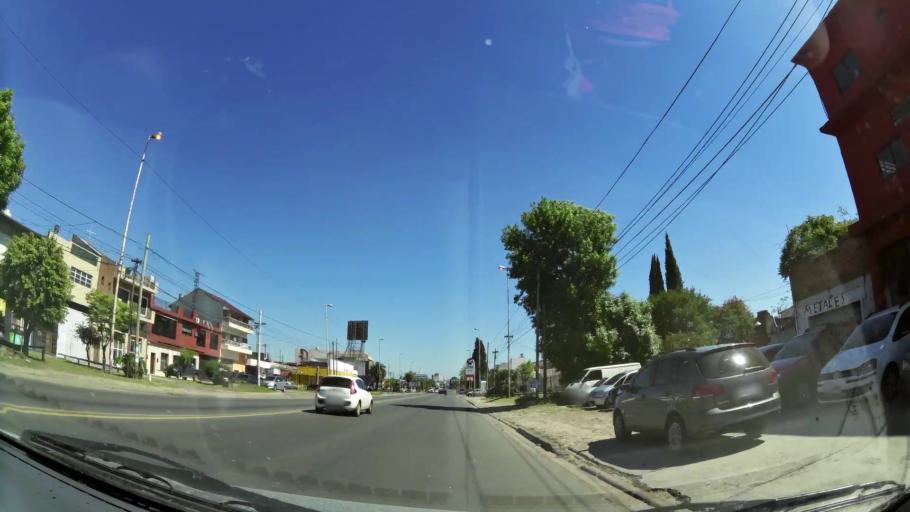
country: AR
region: Buenos Aires
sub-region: Partido de Quilmes
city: Quilmes
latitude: -34.7152
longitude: -58.3060
